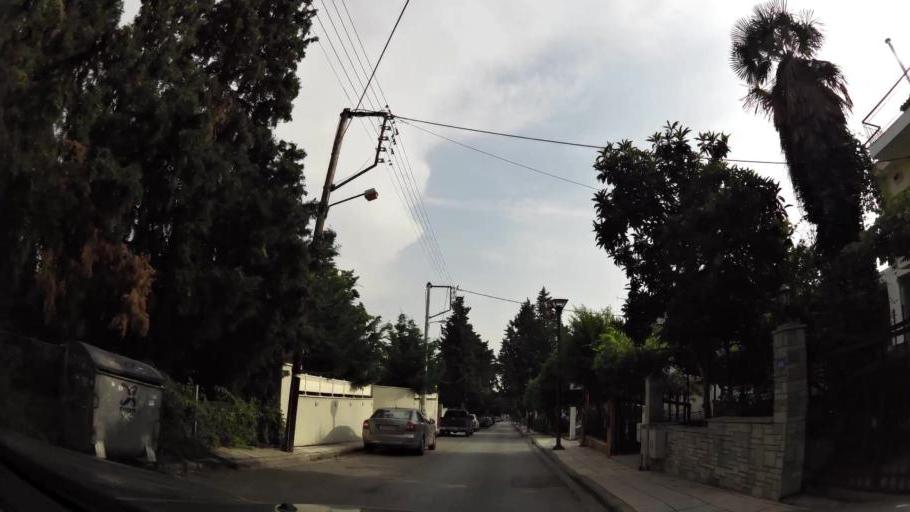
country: GR
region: Central Macedonia
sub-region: Nomos Thessalonikis
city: Oraiokastro
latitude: 40.7286
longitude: 22.9145
